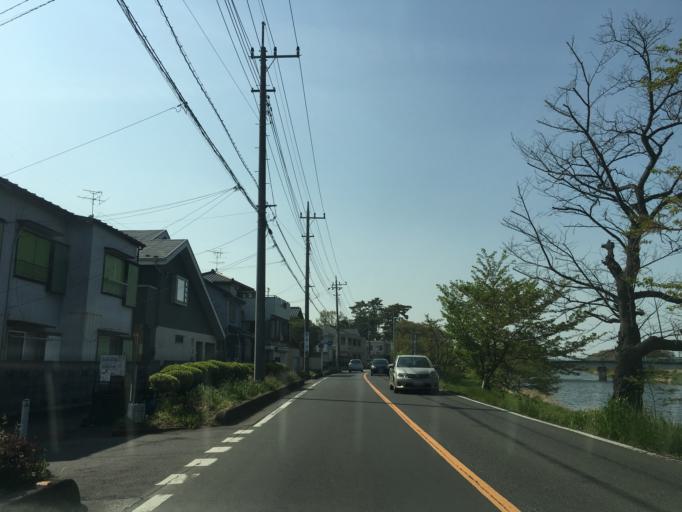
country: JP
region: Saitama
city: Hasuda
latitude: 35.9818
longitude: 139.6617
